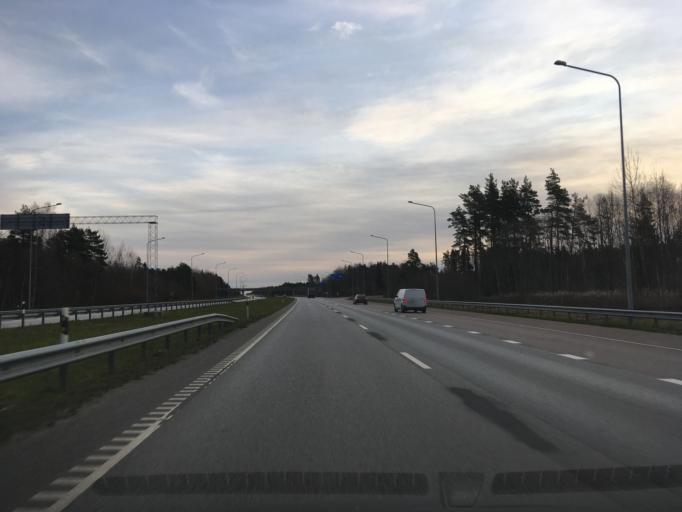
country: EE
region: Harju
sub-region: Raasiku vald
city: Raasiku
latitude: 59.4342
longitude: 25.1819
